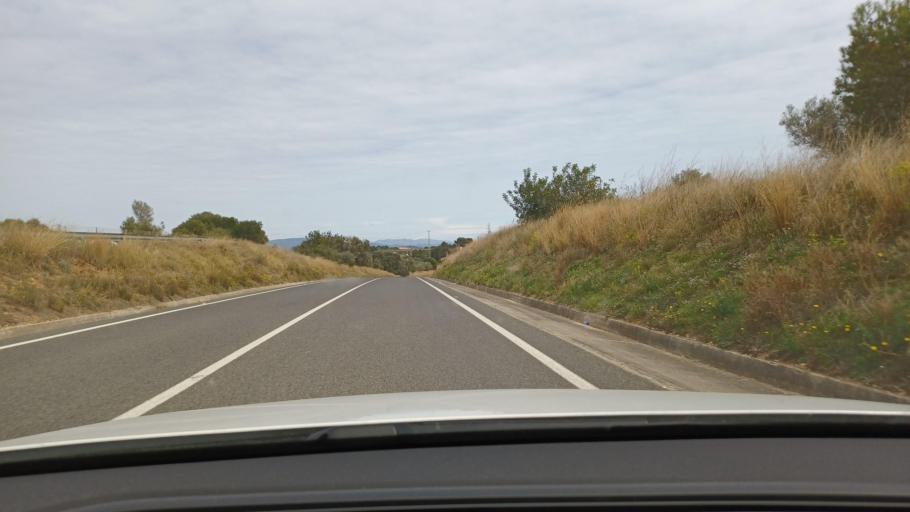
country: ES
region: Catalonia
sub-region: Provincia de Tarragona
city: Masdenverge
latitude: 40.6998
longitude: 0.5435
